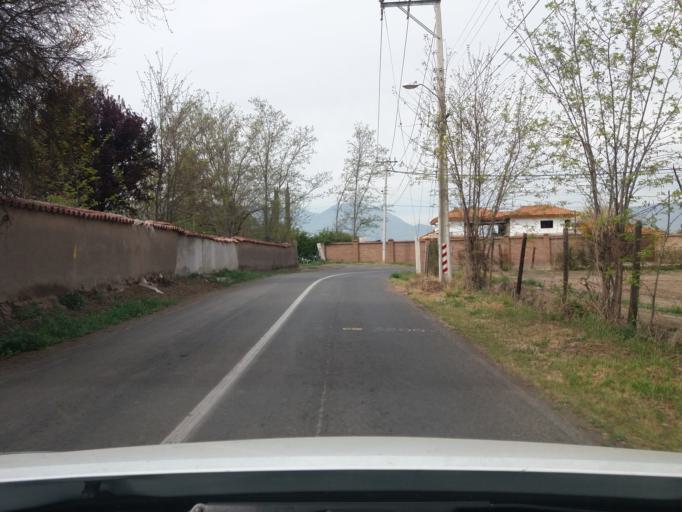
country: CL
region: Valparaiso
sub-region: Provincia de Los Andes
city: Los Andes
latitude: -32.8287
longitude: -70.6584
